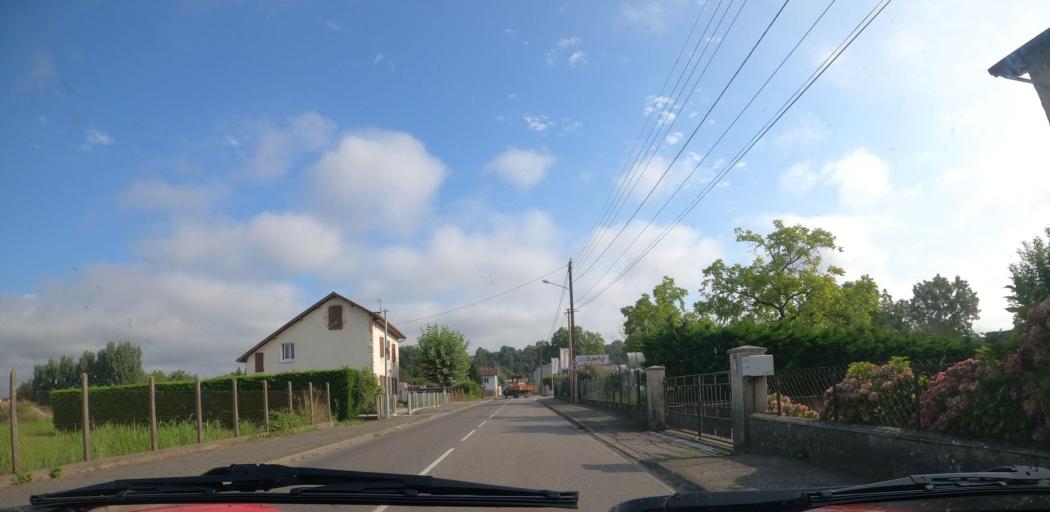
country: FR
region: Aquitaine
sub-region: Departement des Landes
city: Peyrehorade
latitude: 43.5406
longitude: -1.1067
